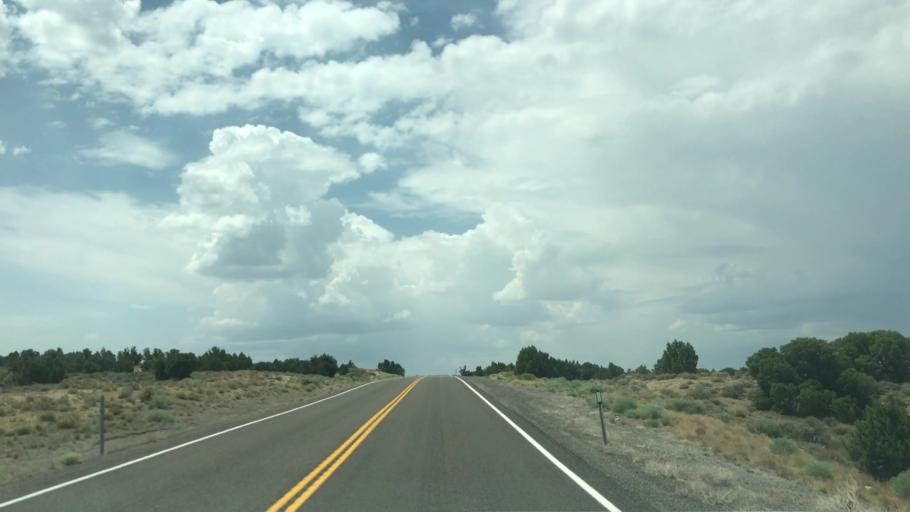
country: US
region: Nevada
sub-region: Eureka County
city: Eureka
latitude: 39.4122
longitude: -115.6937
